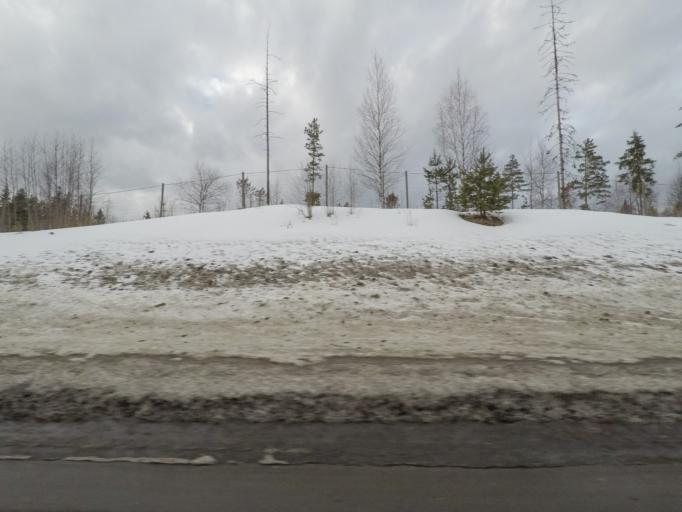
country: FI
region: Paijanne Tavastia
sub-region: Lahti
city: Heinola
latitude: 61.3530
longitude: 26.2230
